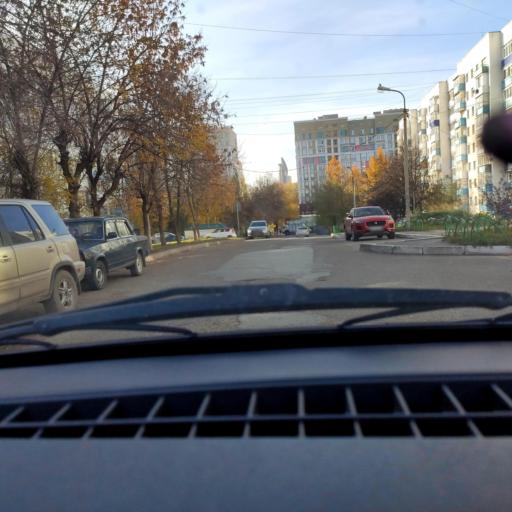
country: RU
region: Bashkortostan
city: Ufa
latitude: 54.7450
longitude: 55.9548
